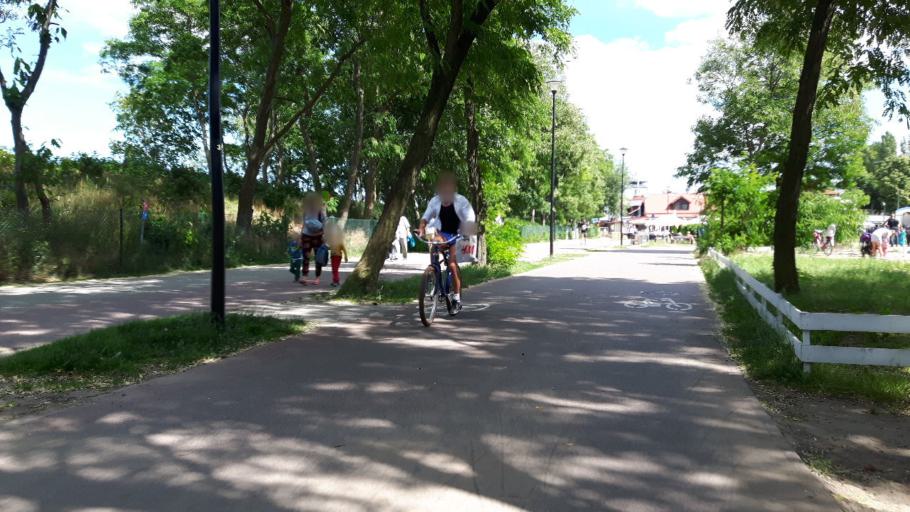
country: PL
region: Pomeranian Voivodeship
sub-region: Gdansk
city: Gdansk
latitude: 54.4117
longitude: 18.6279
